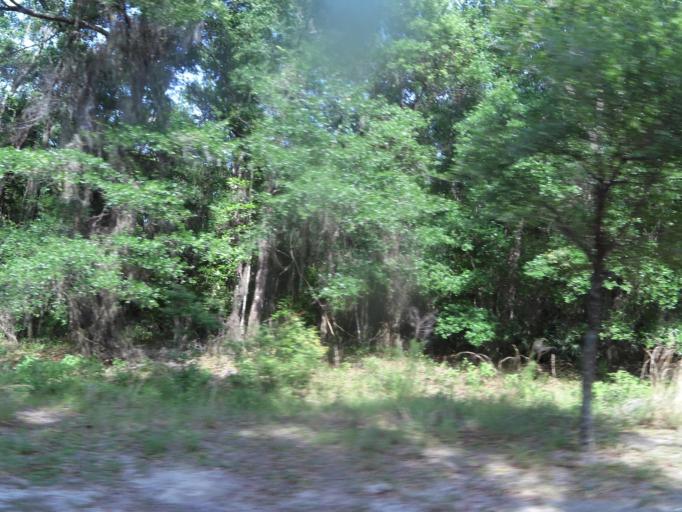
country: US
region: Florida
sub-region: Duval County
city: Atlantic Beach
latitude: 30.4889
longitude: -81.4910
